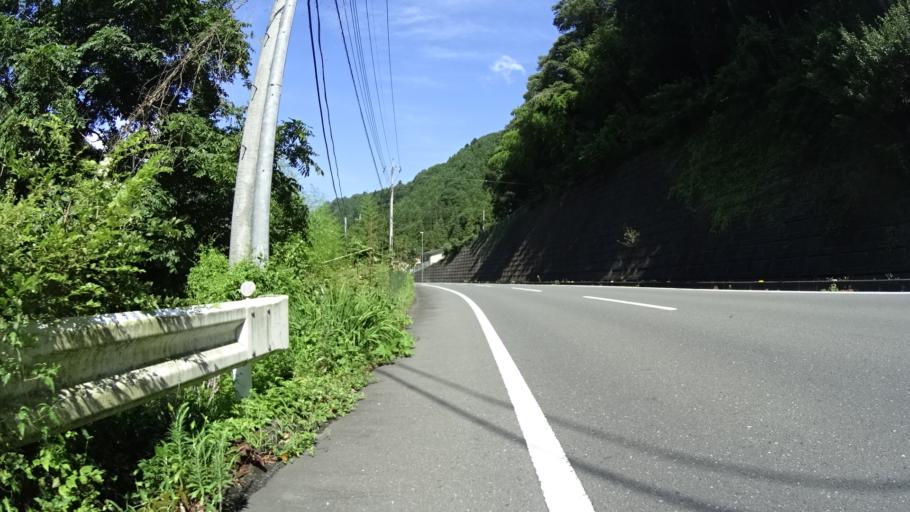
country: JP
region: Saitama
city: Chichibu
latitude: 36.0344
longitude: 138.9267
